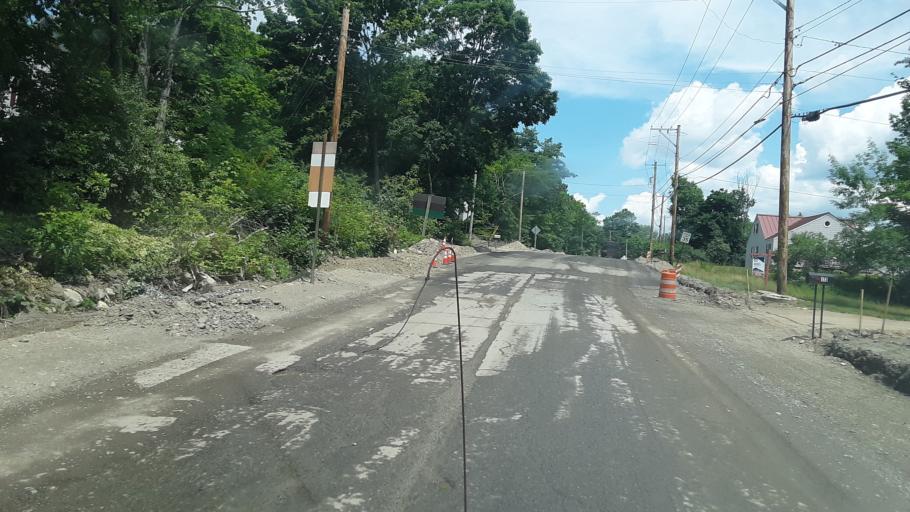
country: US
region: Maine
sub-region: Penobscot County
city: Hampden
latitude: 44.7497
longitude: -68.8309
